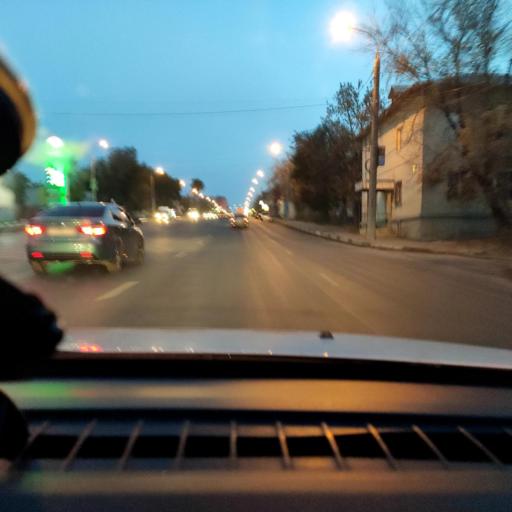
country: RU
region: Samara
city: Samara
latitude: 53.1815
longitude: 50.1918
